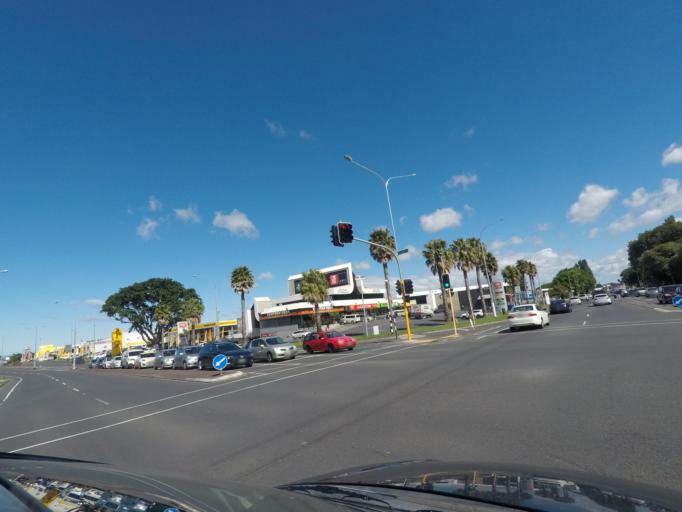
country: NZ
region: Auckland
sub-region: Auckland
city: Manukau City
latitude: -36.9869
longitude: 174.8814
